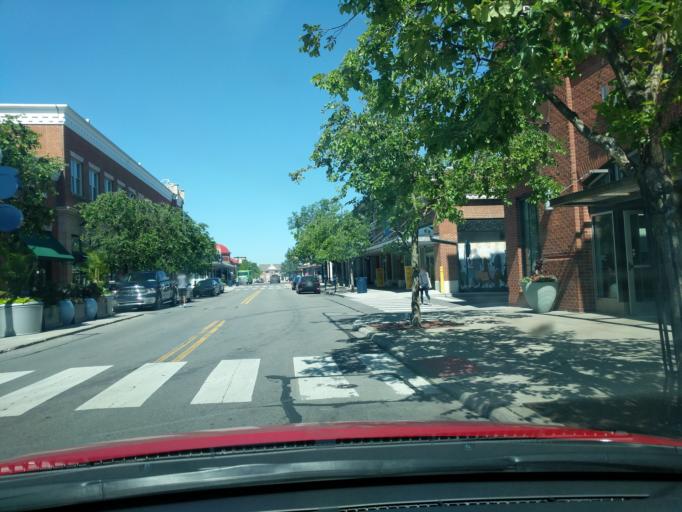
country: US
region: Ohio
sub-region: Franklin County
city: Huber Ridge
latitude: 40.0498
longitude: -82.9141
